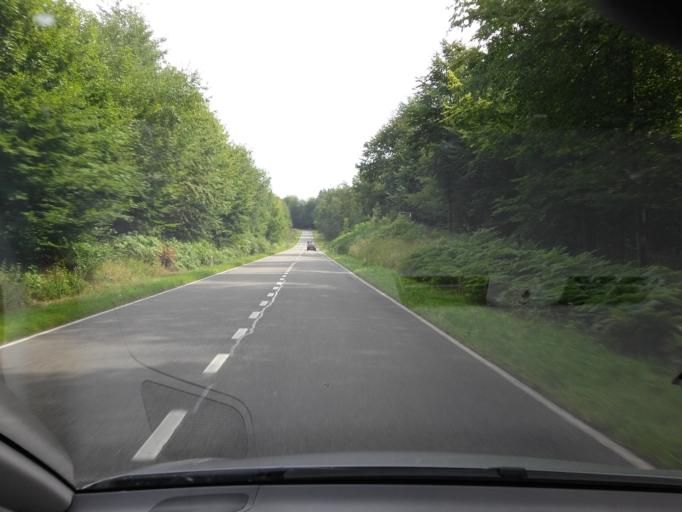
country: BE
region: Wallonia
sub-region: Province du Luxembourg
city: Chiny
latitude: 49.7765
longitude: 5.3295
